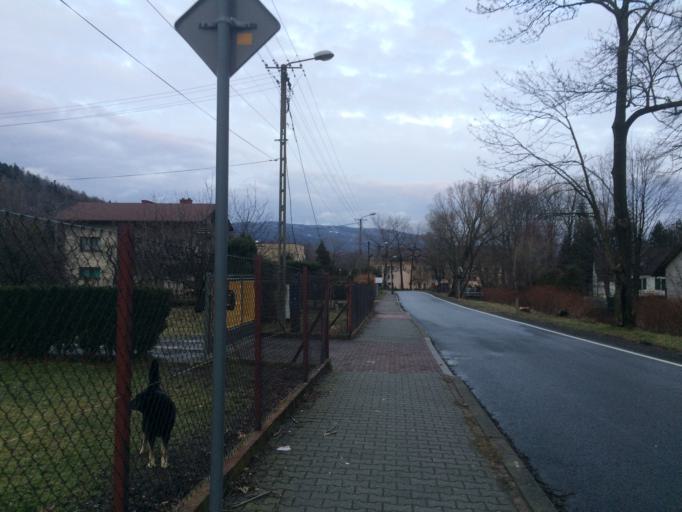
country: PL
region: Silesian Voivodeship
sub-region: Powiat bielski
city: Bystra
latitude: 49.7605
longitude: 19.0537
